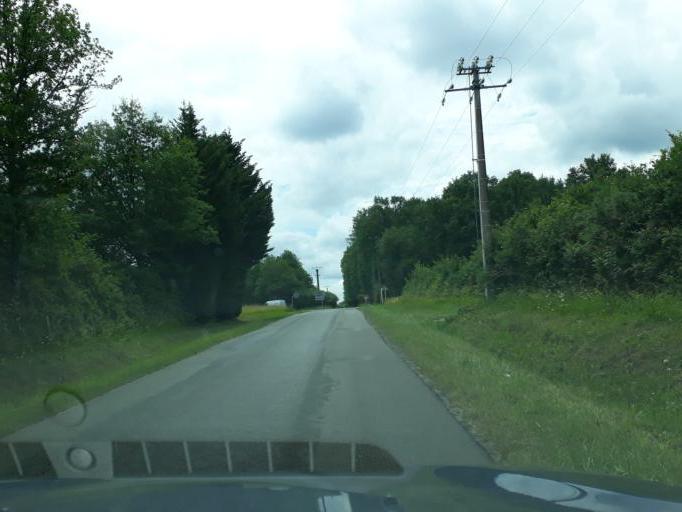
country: FR
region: Centre
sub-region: Departement du Loir-et-Cher
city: Saint-Viatre
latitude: 47.5766
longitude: 1.9524
